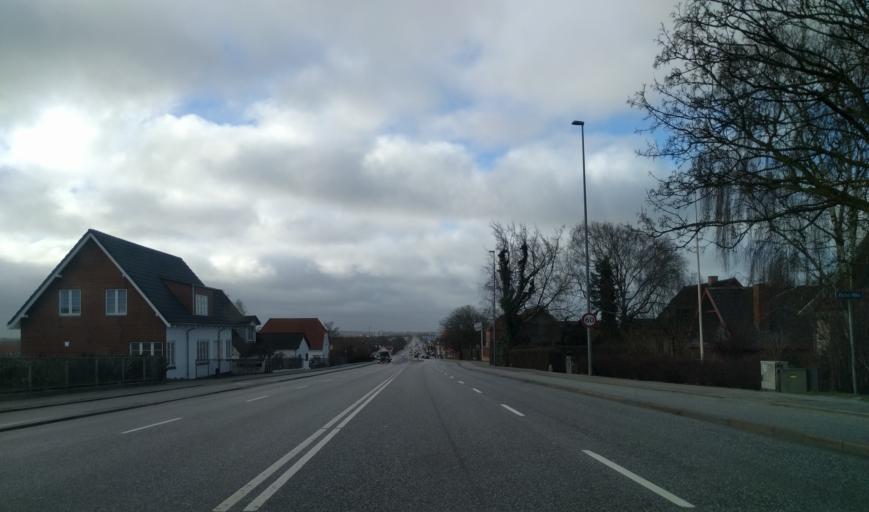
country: DK
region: North Denmark
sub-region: Alborg Kommune
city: Aalborg
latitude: 57.0126
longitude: 9.8906
